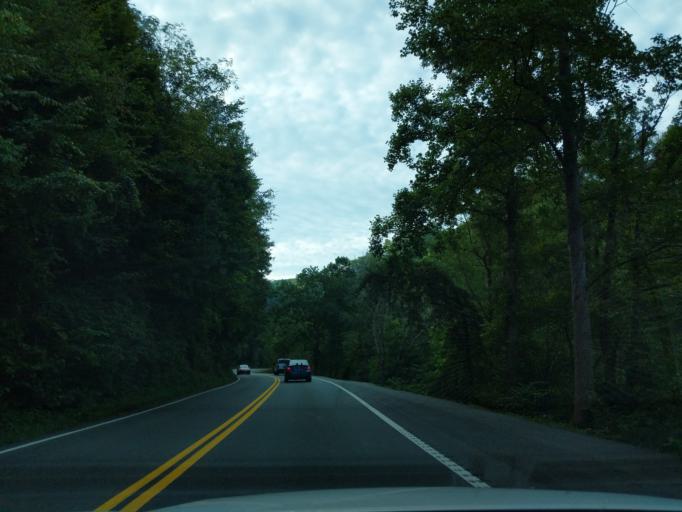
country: US
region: Tennessee
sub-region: Polk County
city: Benton
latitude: 35.0940
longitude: -84.5331
